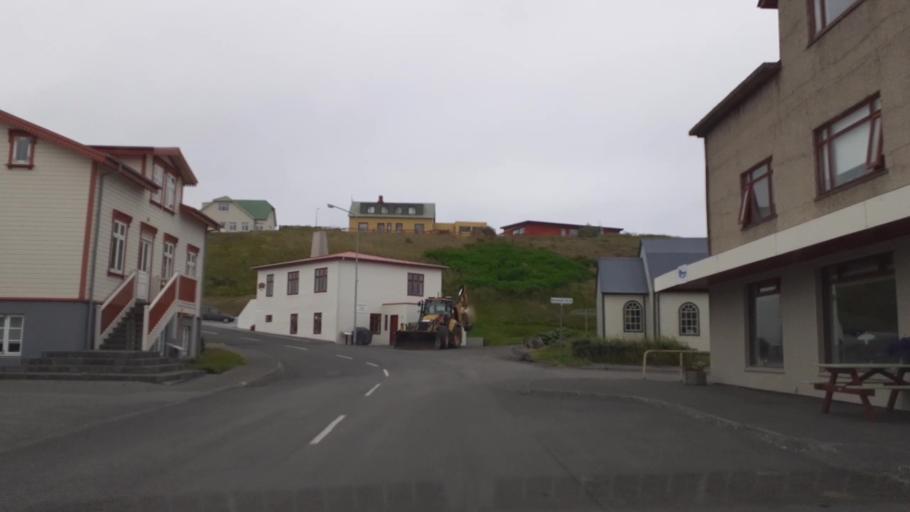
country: IS
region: Northwest
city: Saudarkrokur
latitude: 65.6595
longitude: -20.3015
